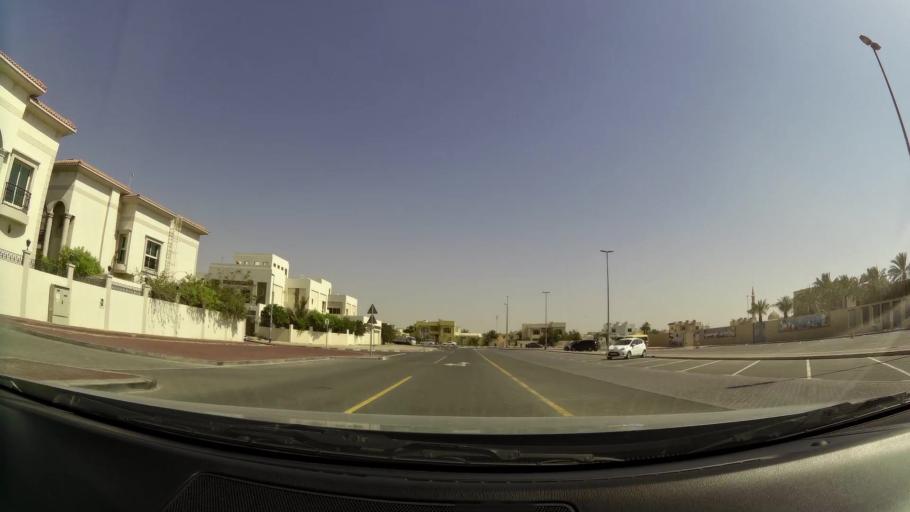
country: AE
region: Dubai
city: Dubai
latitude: 25.1066
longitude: 55.1940
